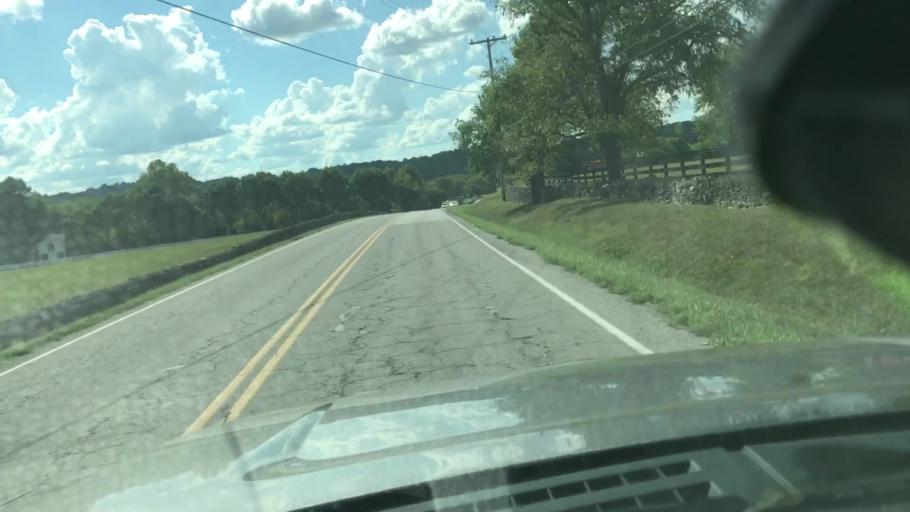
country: US
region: Tennessee
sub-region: Davidson County
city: Forest Hills
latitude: 36.0286
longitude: -86.9129
